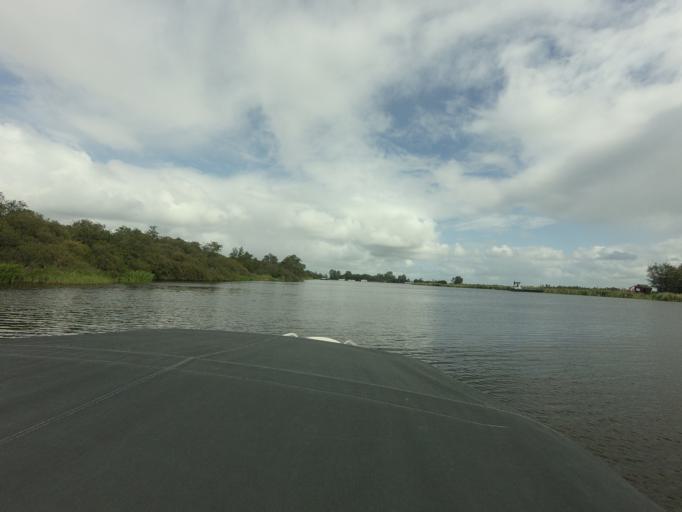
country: NL
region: Friesland
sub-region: Gemeente Boarnsterhim
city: Warten
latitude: 53.1169
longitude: 5.9392
